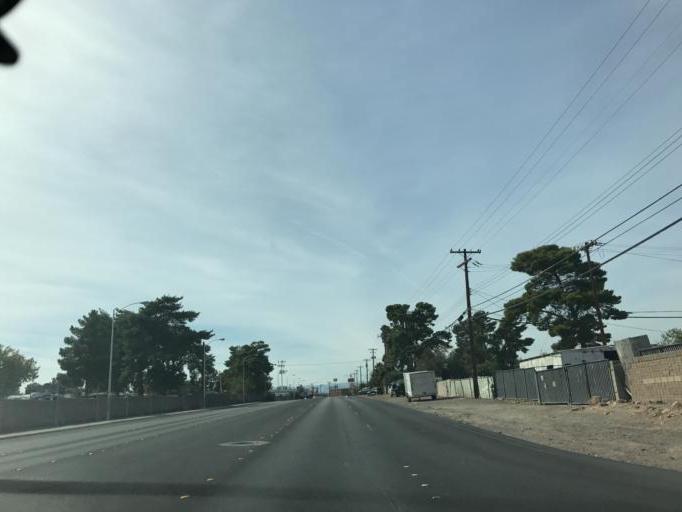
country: US
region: Nevada
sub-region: Clark County
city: Winchester
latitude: 36.1296
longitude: -115.0774
